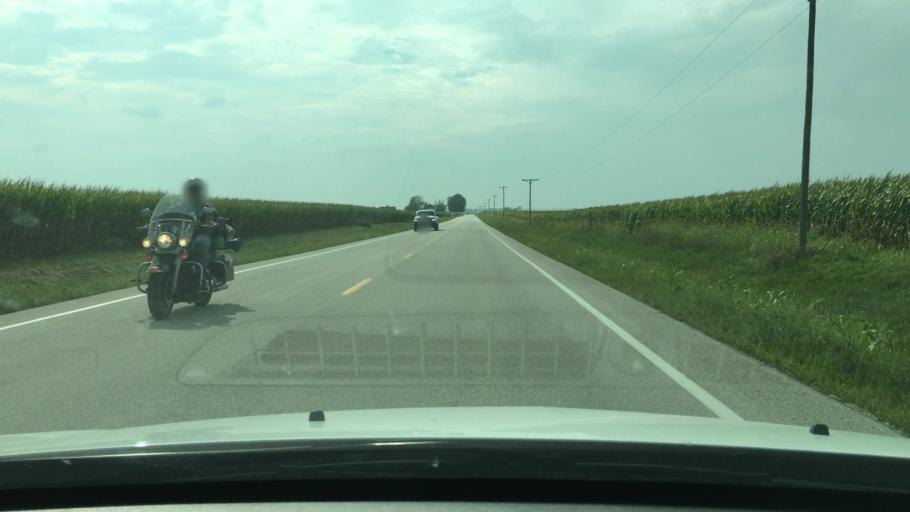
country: US
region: Illinois
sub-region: DeKalb County
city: Waterman
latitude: 41.8491
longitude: -88.7954
